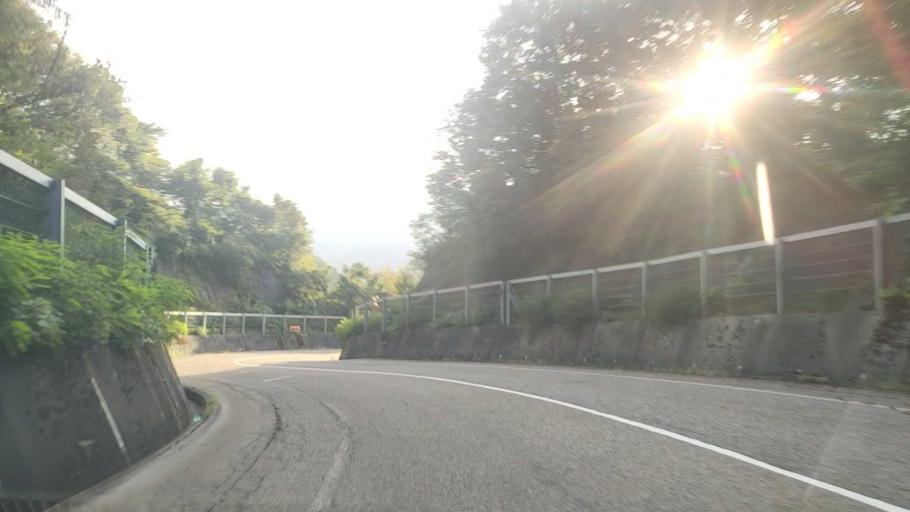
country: JP
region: Toyama
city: Yatsuomachi-higashikumisaka
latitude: 36.4538
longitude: 137.0297
